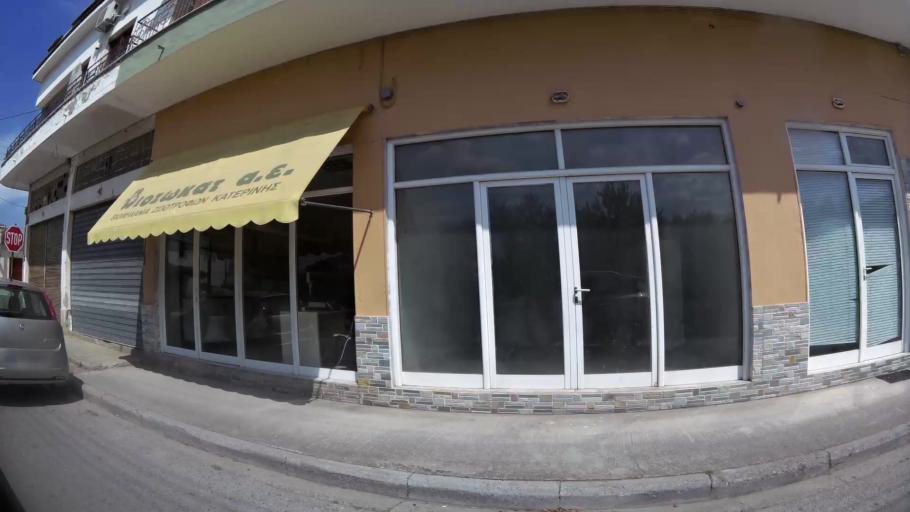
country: GR
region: Central Macedonia
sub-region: Nomos Pierias
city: Korinos
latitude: 40.3160
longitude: 22.5836
